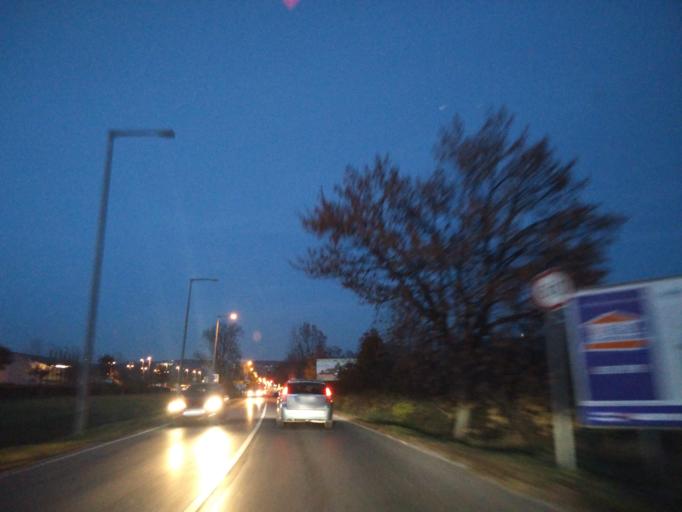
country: HU
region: Pest
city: Budakeszi
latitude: 47.4989
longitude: 18.9173
